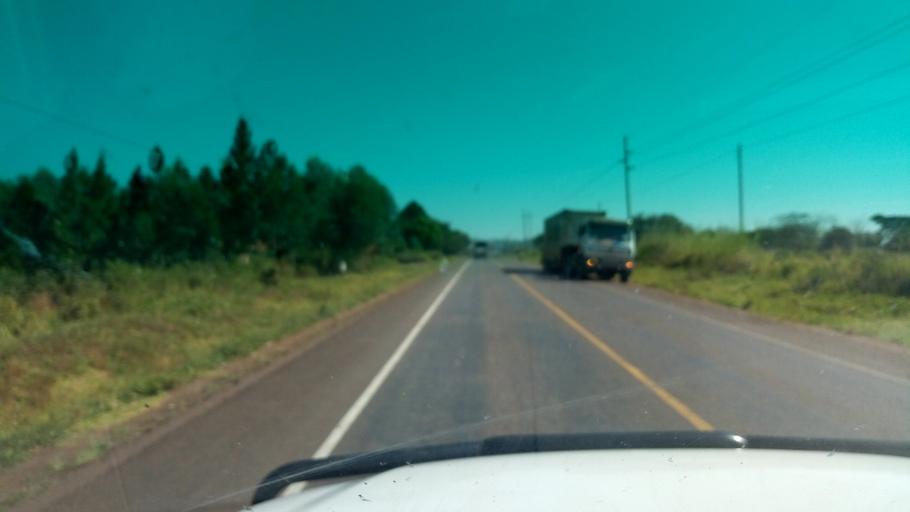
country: UG
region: Western Region
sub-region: Kiryandongo District
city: Kiryandongo
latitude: 1.9362
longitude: 32.1263
